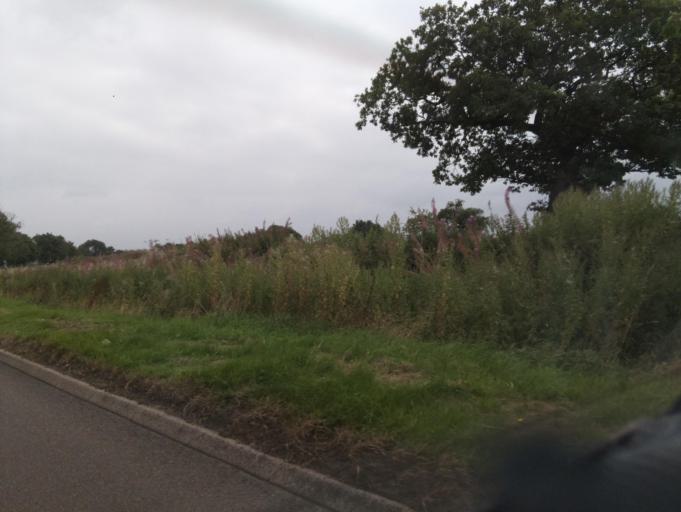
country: GB
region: England
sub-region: Staffordshire
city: Mayfield
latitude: 53.0236
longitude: -1.7873
